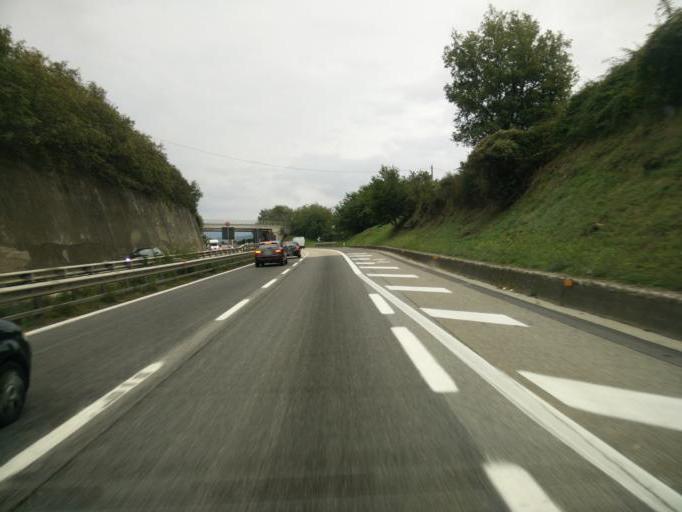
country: IT
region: Tuscany
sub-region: Province of Florence
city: Cavallina
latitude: 43.9920
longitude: 11.2189
